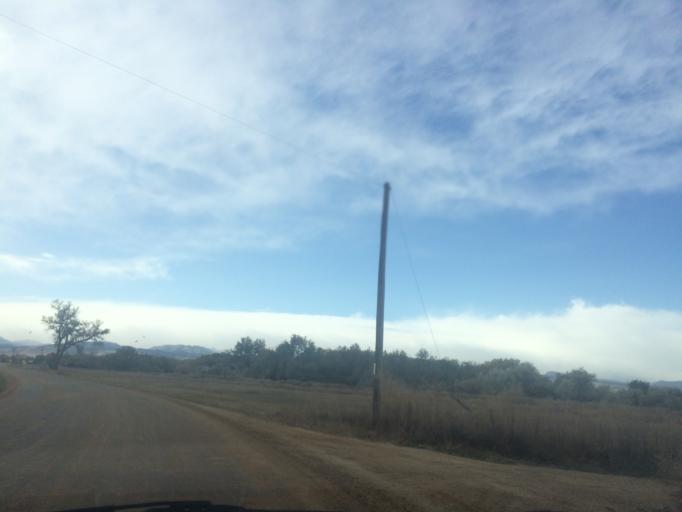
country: US
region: Colorado
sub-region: Boulder County
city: Niwot
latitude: 40.1234
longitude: -105.1451
